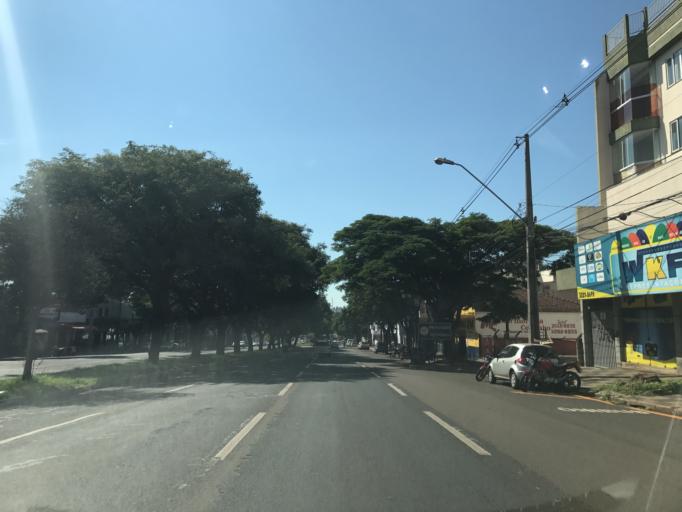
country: BR
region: Parana
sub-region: Maringa
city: Maringa
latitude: -23.4153
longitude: -51.9523
